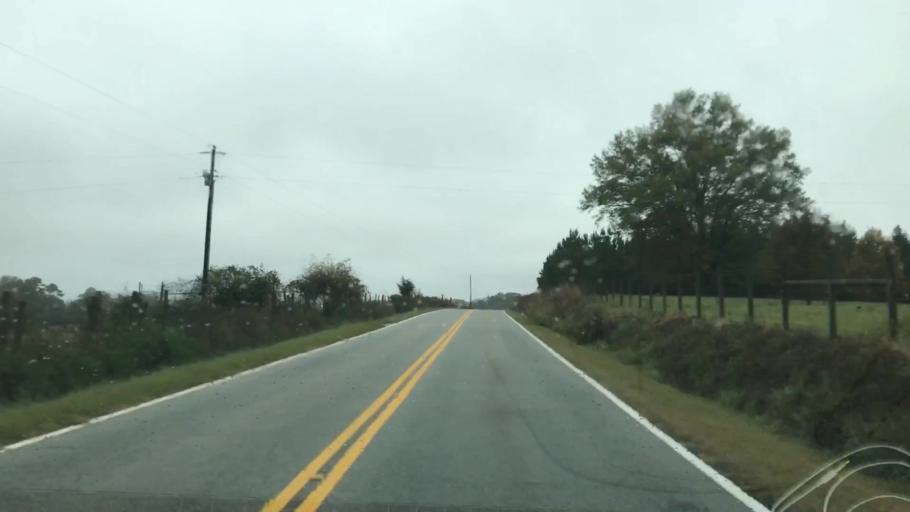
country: US
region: South Carolina
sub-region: Laurens County
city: Joanna
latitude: 34.3599
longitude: -81.7918
